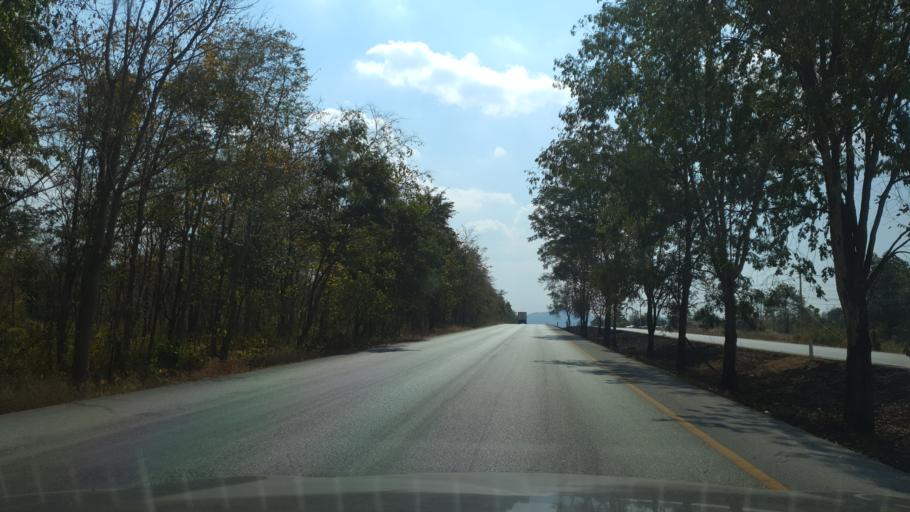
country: TH
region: Lampang
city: Mae Phrik
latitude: 17.3887
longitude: 99.1486
